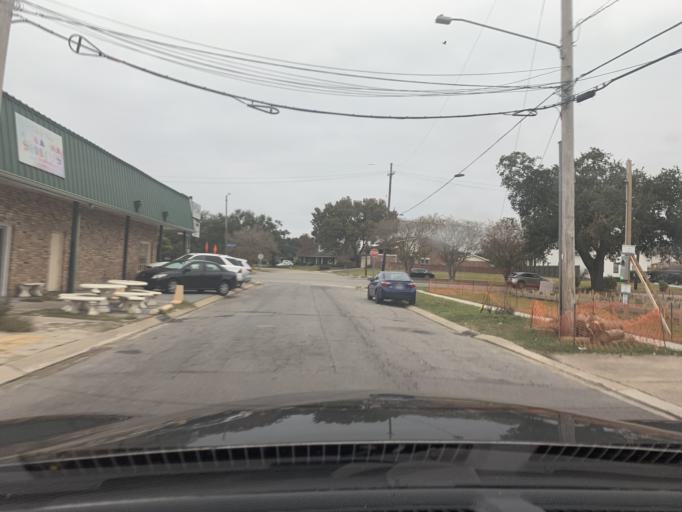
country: US
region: Louisiana
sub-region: Jefferson Parish
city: Metairie
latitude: 30.0189
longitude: -90.1051
